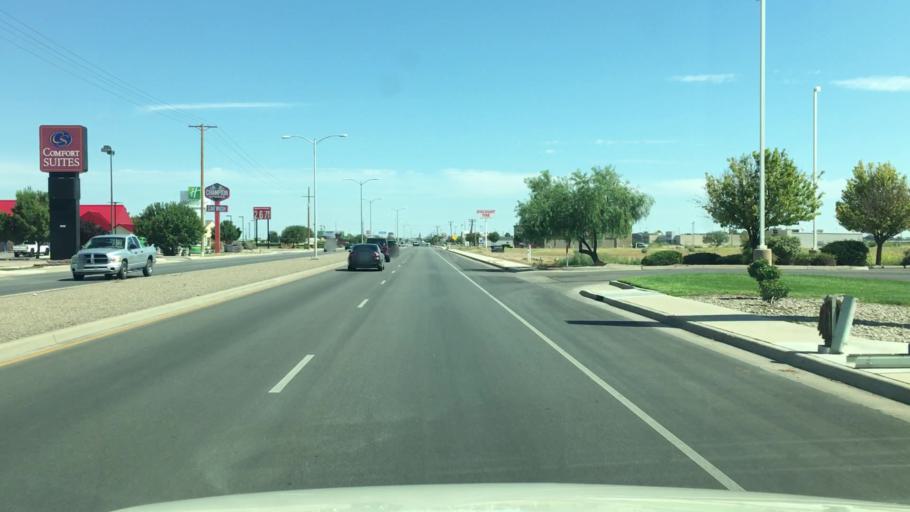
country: US
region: New Mexico
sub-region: Chaves County
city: Roswell
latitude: 33.4418
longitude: -104.5232
